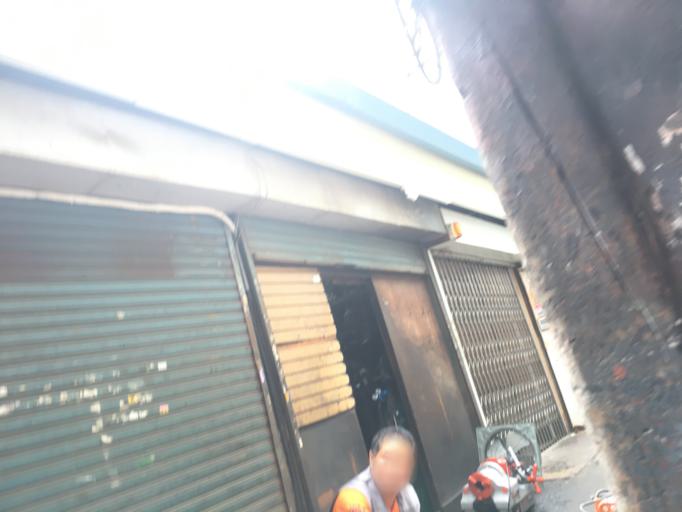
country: KR
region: Seoul
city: Seoul
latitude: 37.5678
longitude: 126.9913
